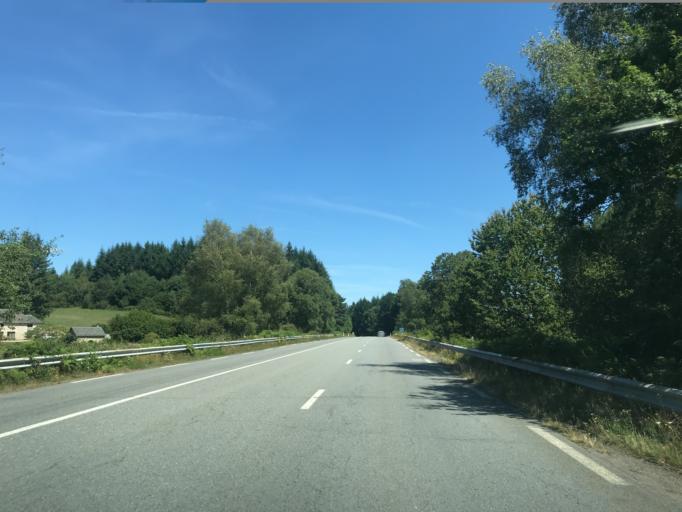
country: FR
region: Limousin
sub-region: Departement de la Correze
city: Egletons
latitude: 45.3620
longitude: 1.9884
